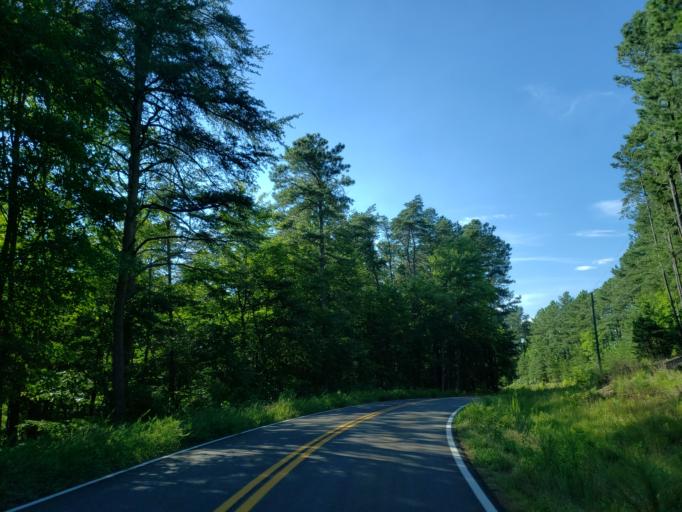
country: US
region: Georgia
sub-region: Bartow County
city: Rydal
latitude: 34.3601
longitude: -84.6150
